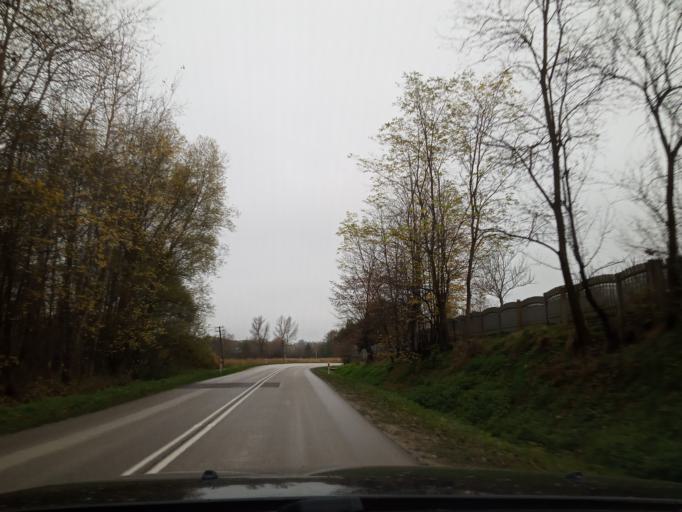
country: PL
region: Swietokrzyskie
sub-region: Powiat pinczowski
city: Dzialoszyce
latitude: 50.3934
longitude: 20.3274
